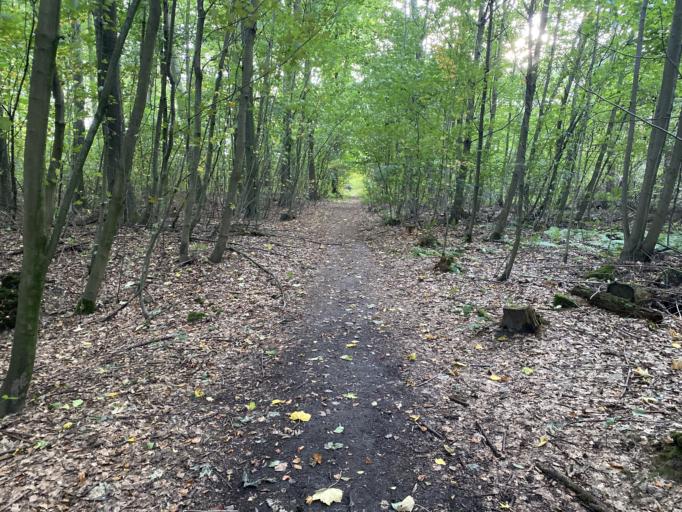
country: DE
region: North Rhine-Westphalia
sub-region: Regierungsbezirk Detmold
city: Kirchlengern
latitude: 52.1773
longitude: 8.6416
